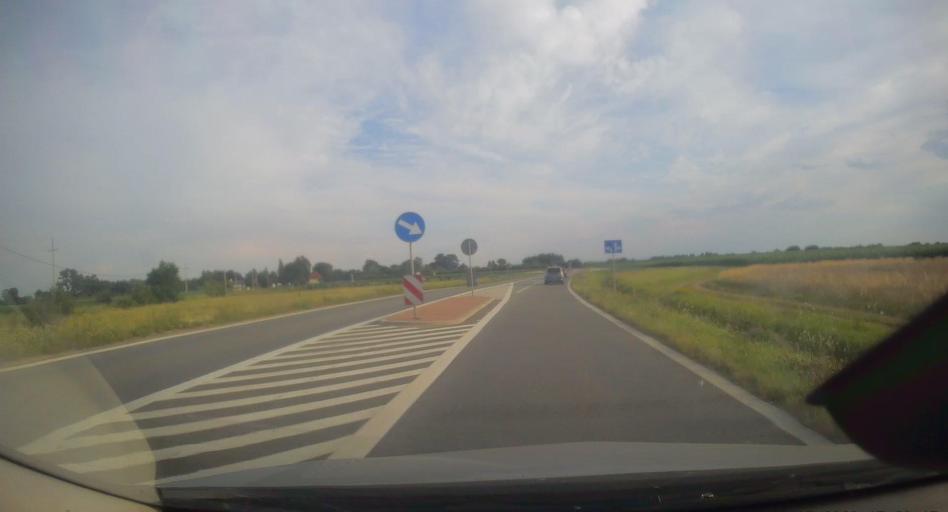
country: PL
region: Lesser Poland Voivodeship
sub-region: Powiat brzeski
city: Szczurowa
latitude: 50.1439
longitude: 20.6132
